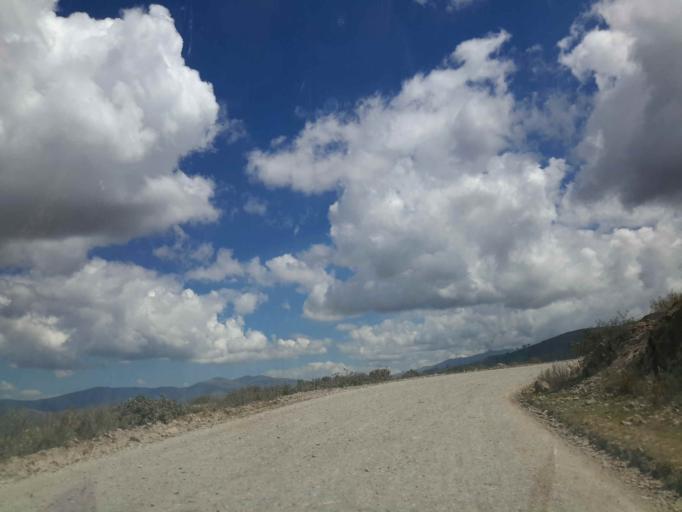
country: PE
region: Apurimac
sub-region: Provincia de Andahuaylas
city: San Jeronimo
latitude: -13.6388
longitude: -73.3368
